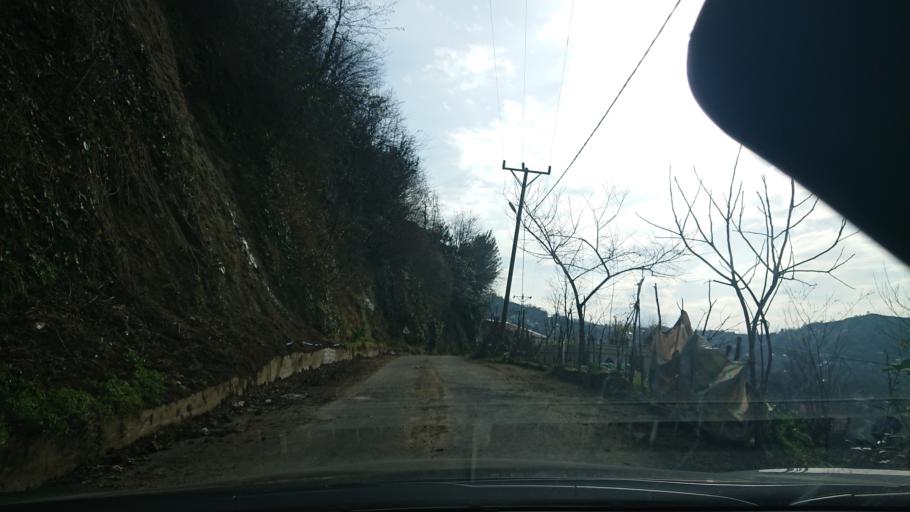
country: TR
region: Rize
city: Rize
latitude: 40.9900
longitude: 40.4924
